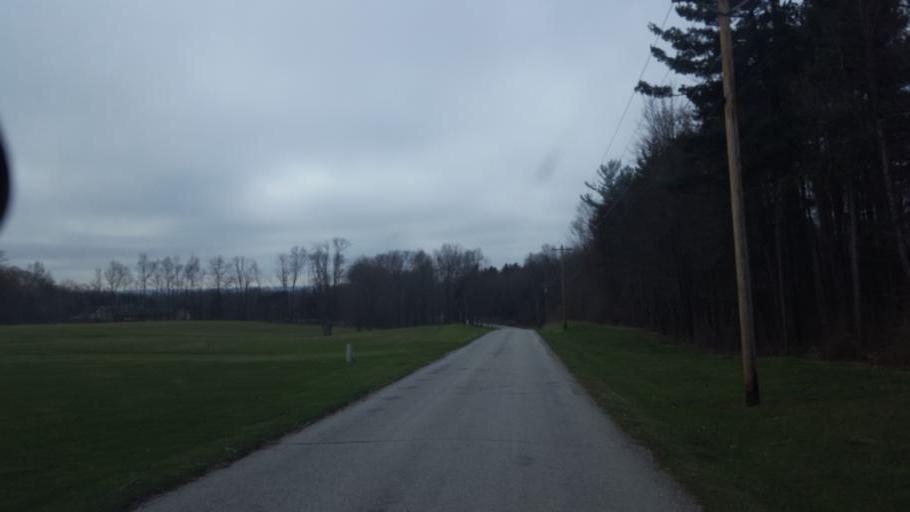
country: US
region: Ohio
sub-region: Knox County
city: Fredericktown
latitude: 40.4857
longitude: -82.6463
